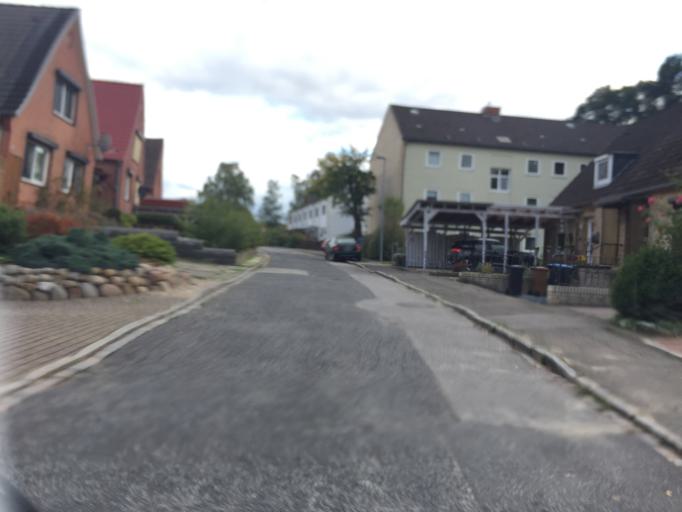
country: DE
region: Schleswig-Holstein
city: Itzehoe
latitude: 53.9391
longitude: 9.5037
